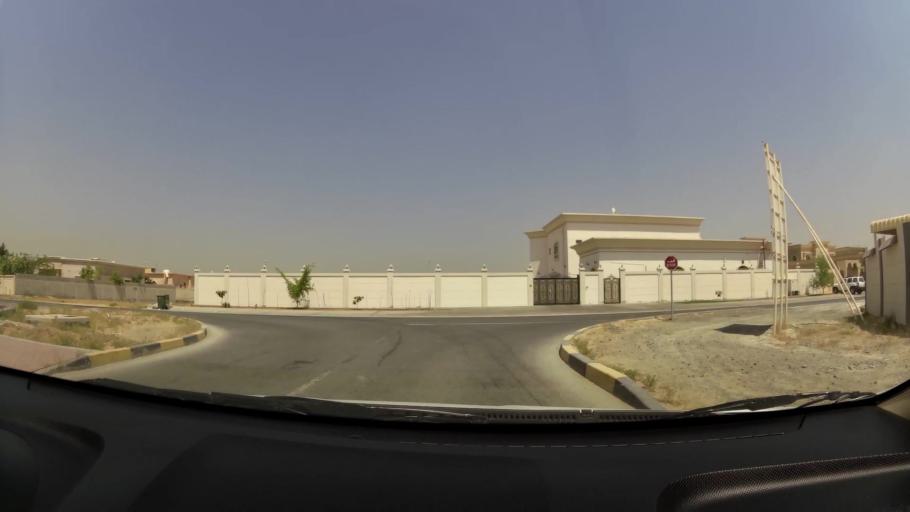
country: AE
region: Ajman
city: Ajman
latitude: 25.4173
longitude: 55.5148
